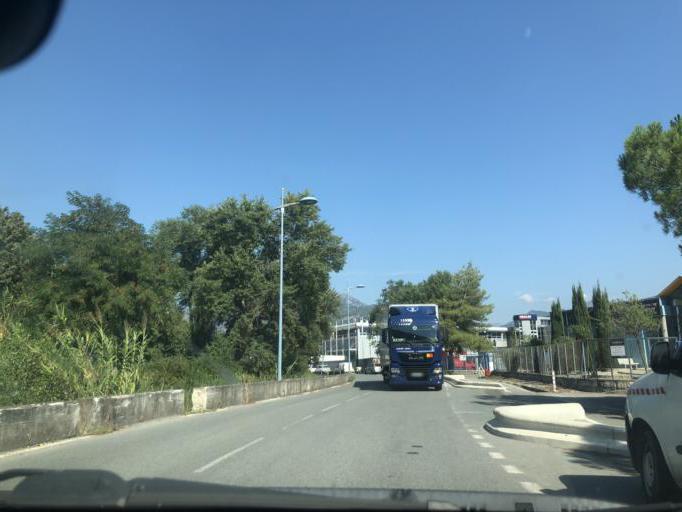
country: FR
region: Provence-Alpes-Cote d'Azur
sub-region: Departement des Alpes-Maritimes
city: Saint-Martin-du-Var
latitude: 43.8061
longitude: 7.1859
